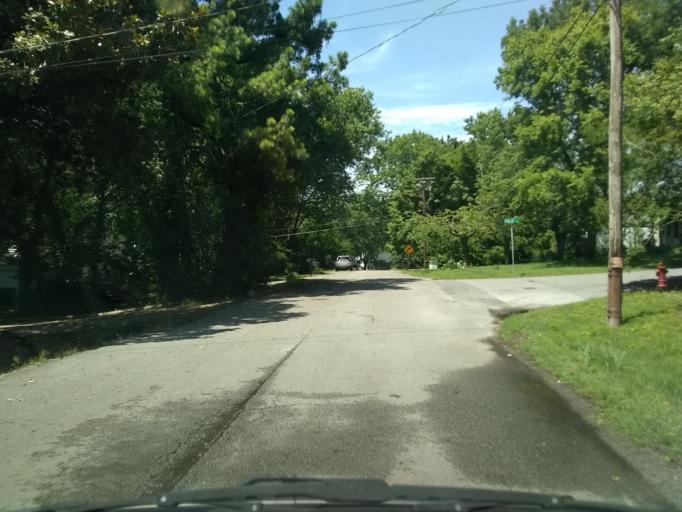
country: US
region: Tennessee
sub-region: Davidson County
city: Oak Hill
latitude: 36.1281
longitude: -86.7049
